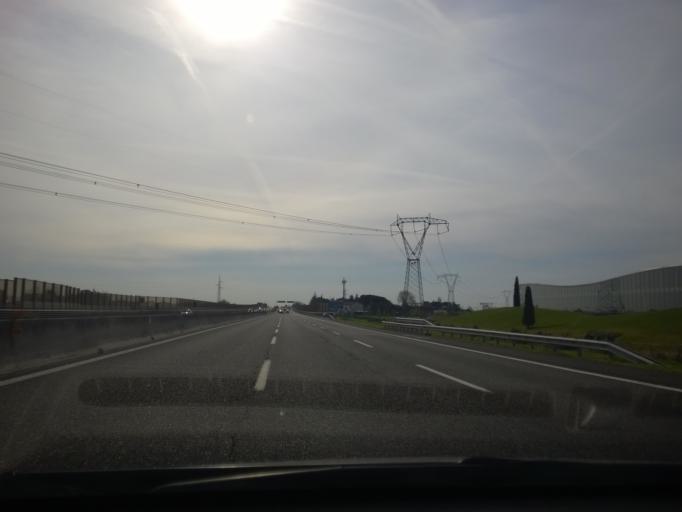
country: IT
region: Emilia-Romagna
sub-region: Forli-Cesena
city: Cesena
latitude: 44.1724
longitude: 12.2774
